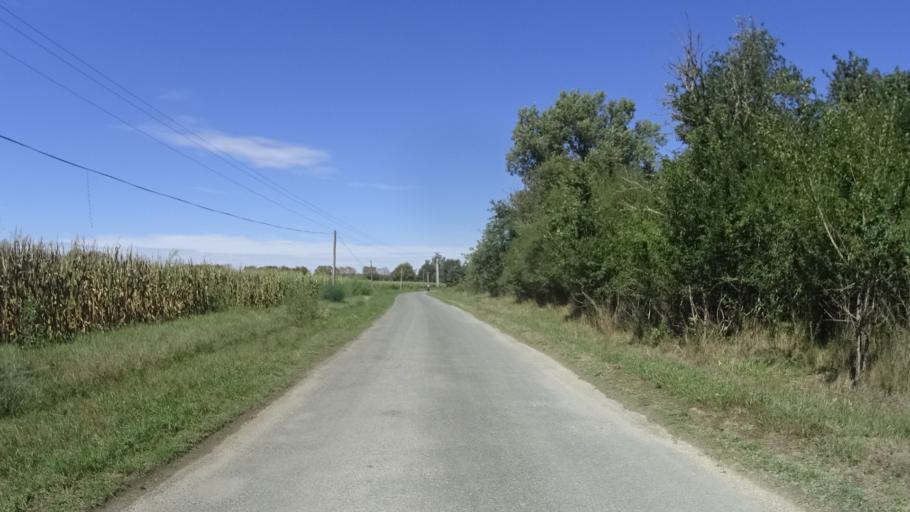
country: FR
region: Centre
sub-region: Departement du Loiret
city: Bonny-sur-Loire
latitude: 47.5467
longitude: 2.8343
